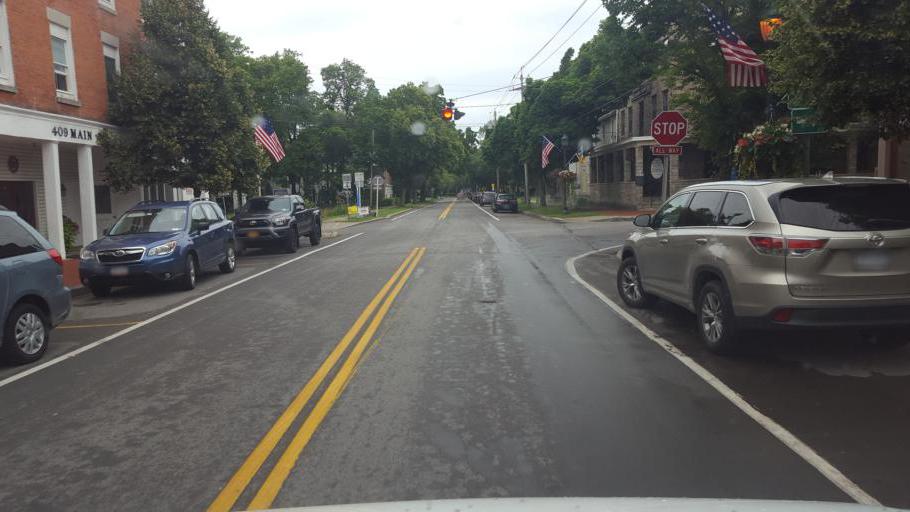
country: US
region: New York
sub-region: Niagara County
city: Youngstown
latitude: 43.2503
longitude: -79.0499
